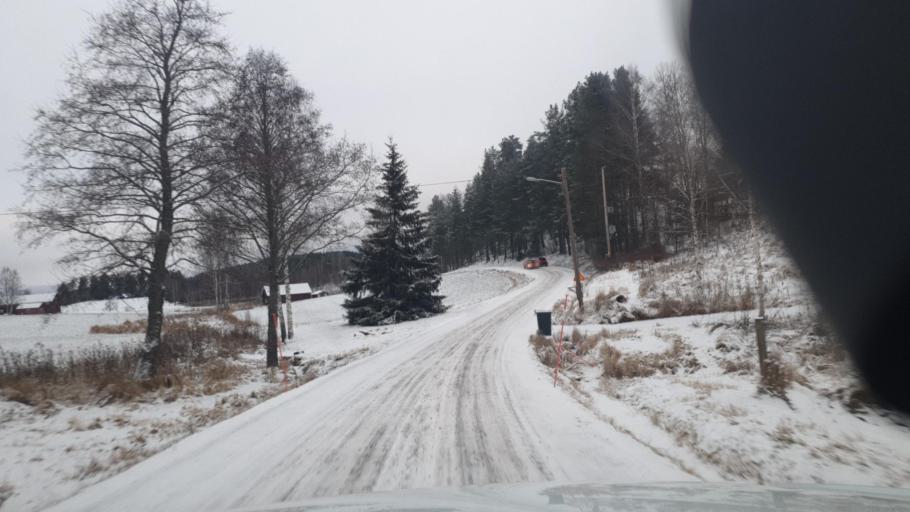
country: SE
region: Vaermland
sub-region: Karlstads Kommun
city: Edsvalla
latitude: 59.6086
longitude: 13.0662
